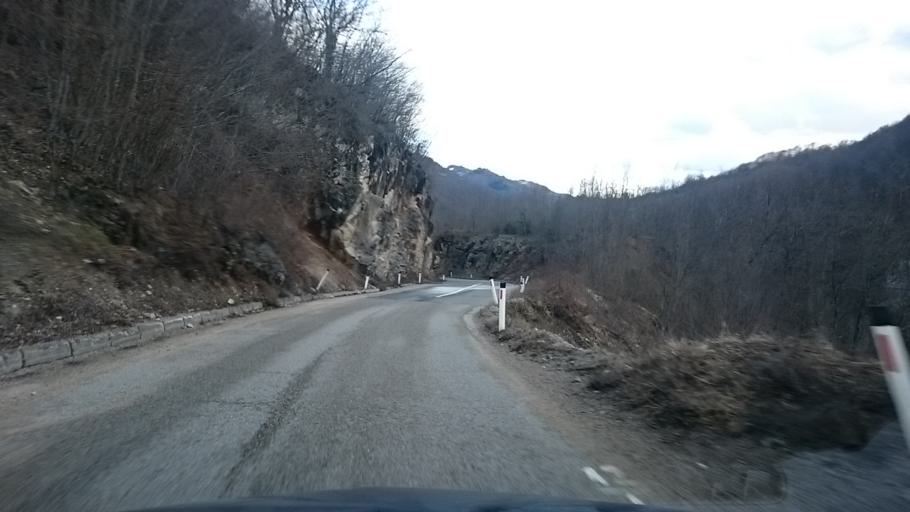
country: BA
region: Republika Srpska
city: Skender Vakuf
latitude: 44.4440
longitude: 17.3808
